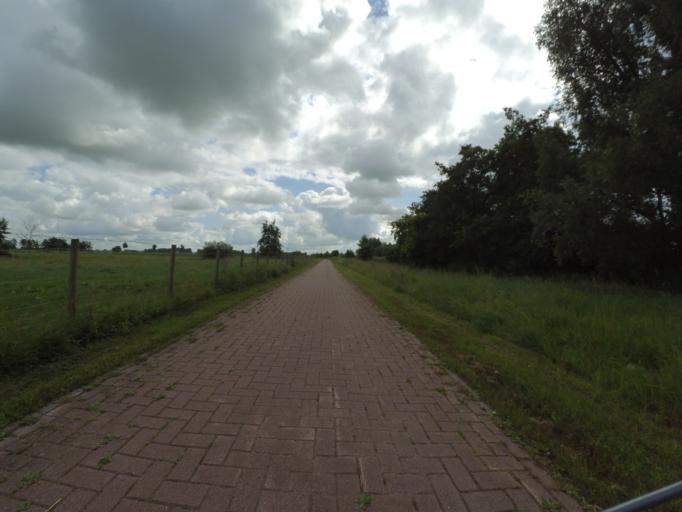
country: NL
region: Friesland
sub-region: Gemeente Achtkarspelen
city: Buitenpost
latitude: 53.2567
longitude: 6.1480
